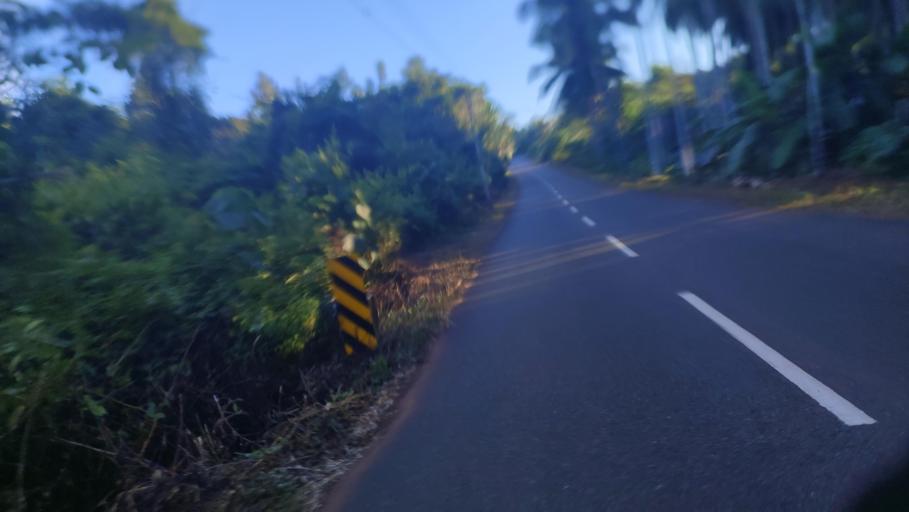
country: IN
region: Kerala
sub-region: Kasaragod District
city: Kasaragod
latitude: 12.4517
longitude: 75.0992
